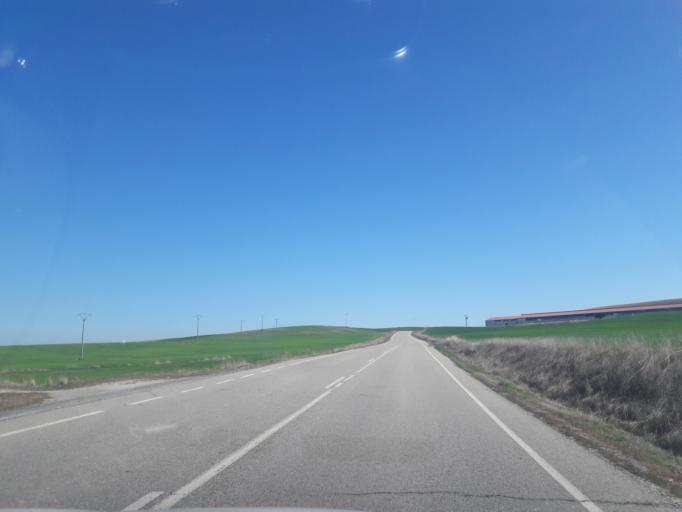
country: ES
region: Castille and Leon
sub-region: Provincia de Salamanca
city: Salmoral
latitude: 40.8113
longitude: -5.2168
